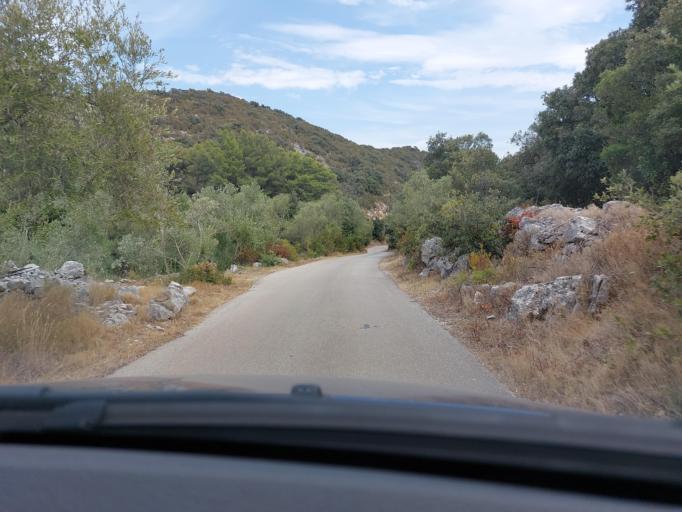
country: HR
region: Dubrovacko-Neretvanska
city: Smokvica
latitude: 42.7614
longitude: 16.9141
